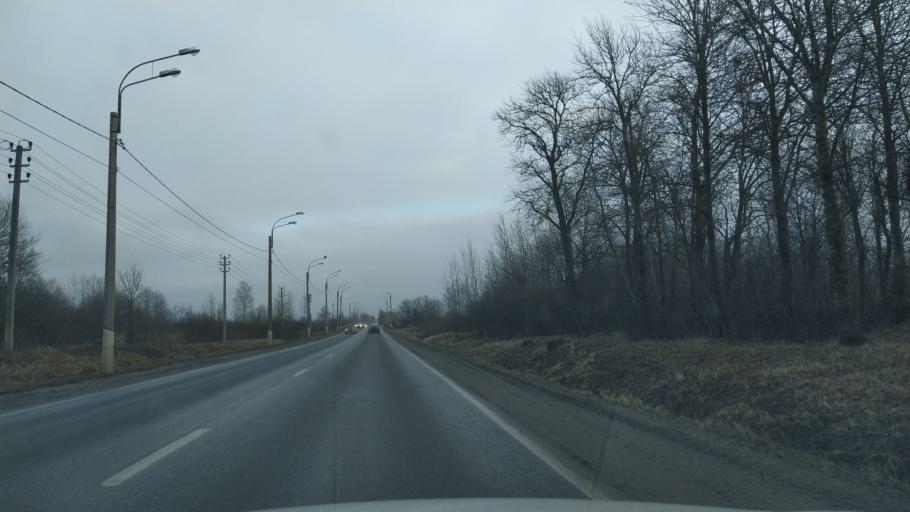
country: RU
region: St.-Petersburg
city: Aleksandrovskaya
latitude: 59.7128
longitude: 30.3074
